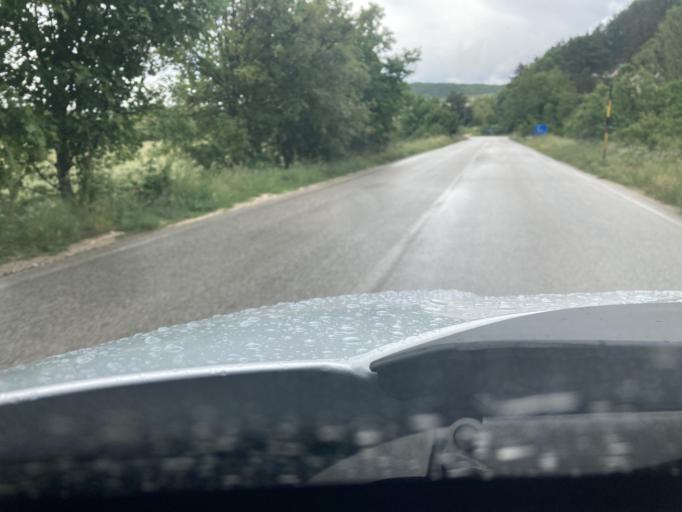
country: IT
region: Abruzzo
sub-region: Provincia dell' Aquila
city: Rocca di Mezzo
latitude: 42.2114
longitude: 13.5207
